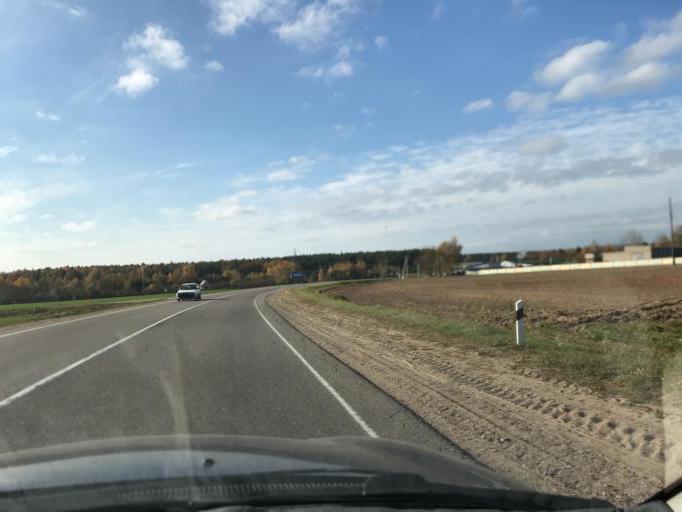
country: BY
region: Grodnenskaya
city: Voranava
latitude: 54.1410
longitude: 25.3208
